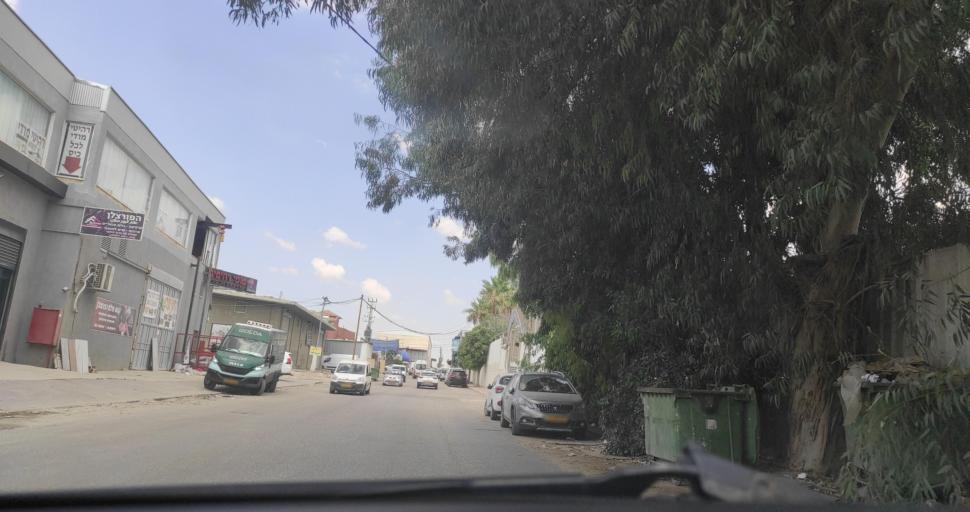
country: IL
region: Central District
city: Rosh Ha'Ayin
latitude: 32.1149
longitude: 34.9561
